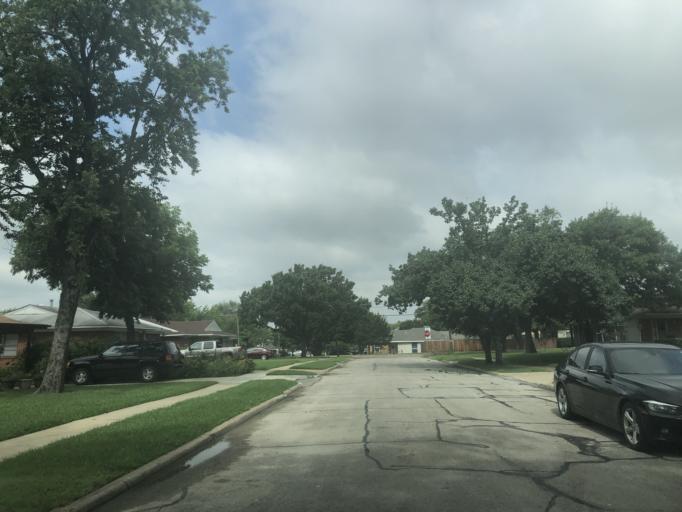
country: US
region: Texas
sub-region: Dallas County
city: Irving
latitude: 32.8068
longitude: -96.9603
